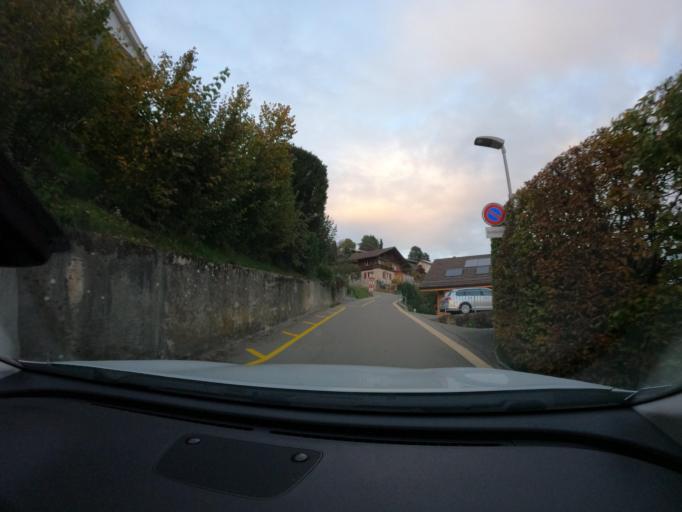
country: CH
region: Bern
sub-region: Bern-Mittelland District
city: Stettlen
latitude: 46.9600
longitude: 7.5274
